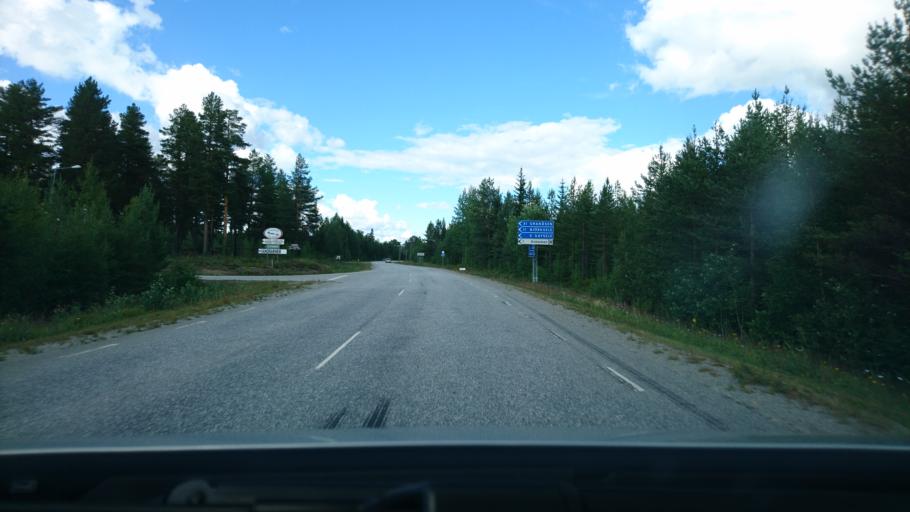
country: SE
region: Vaesterbotten
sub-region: Asele Kommun
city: Asele
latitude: 64.0033
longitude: 17.2736
